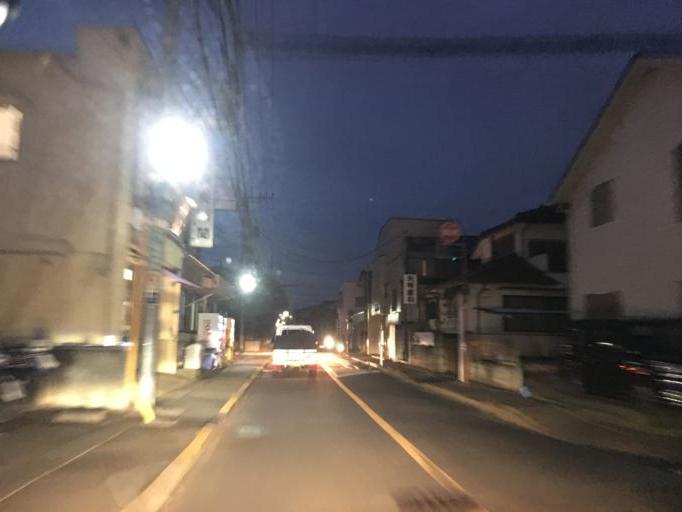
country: JP
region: Tokyo
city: Higashimurayama-shi
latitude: 35.7501
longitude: 139.4493
